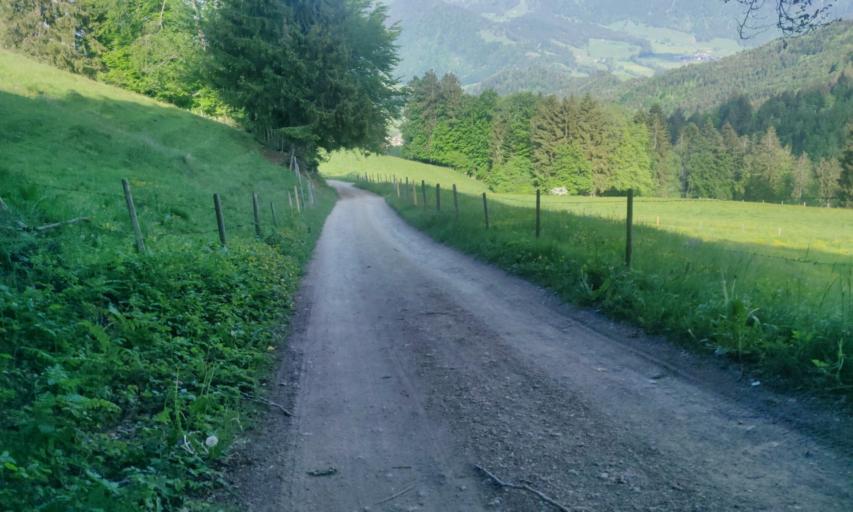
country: CH
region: Fribourg
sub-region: Gruyere District
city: Gruyeres
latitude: 46.5772
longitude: 7.0489
